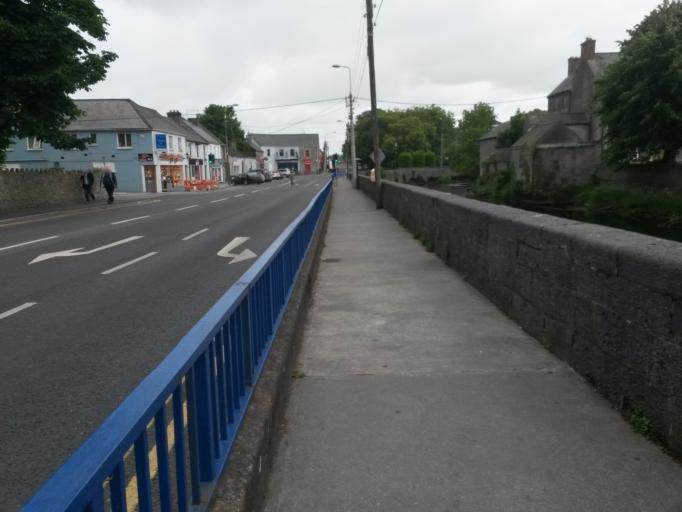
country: IE
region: Munster
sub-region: An Clar
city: Ennis
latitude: 52.8467
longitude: -8.9822
